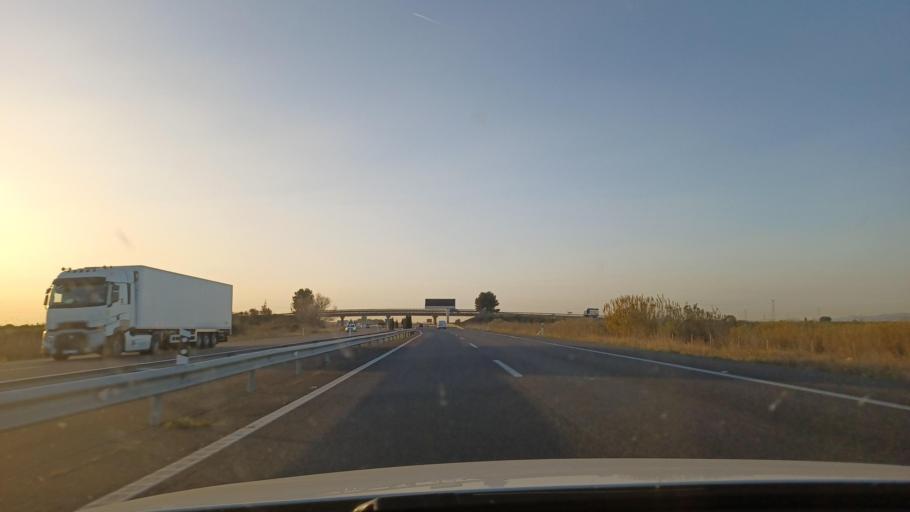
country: ES
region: Valencia
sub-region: Provincia de Castello
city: Alquerias del Nino Perdido
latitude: 39.9079
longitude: -0.1350
